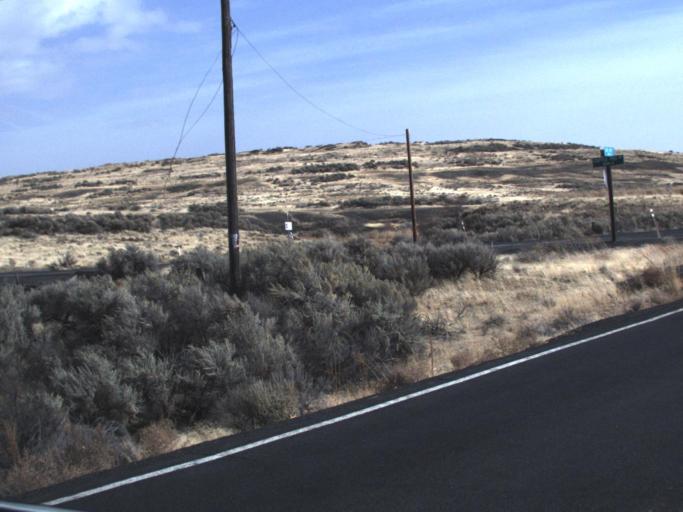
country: US
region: Washington
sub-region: Adams County
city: Ritzville
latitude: 47.4166
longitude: -118.6851
